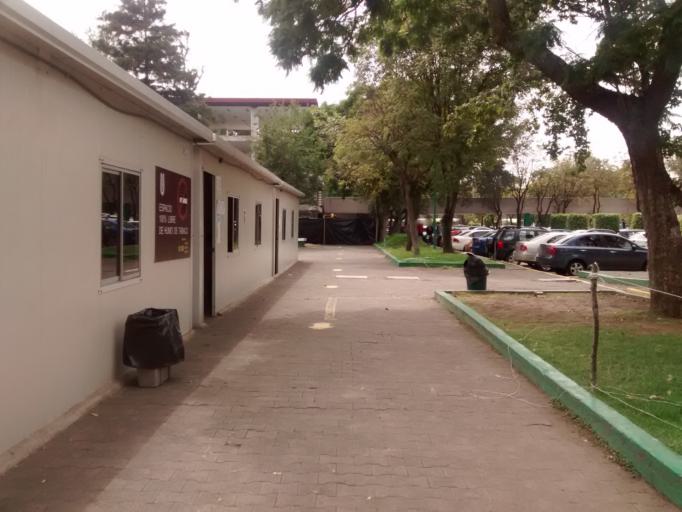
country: MX
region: Mexico City
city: Coyoacan
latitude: 19.3304
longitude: -99.1122
